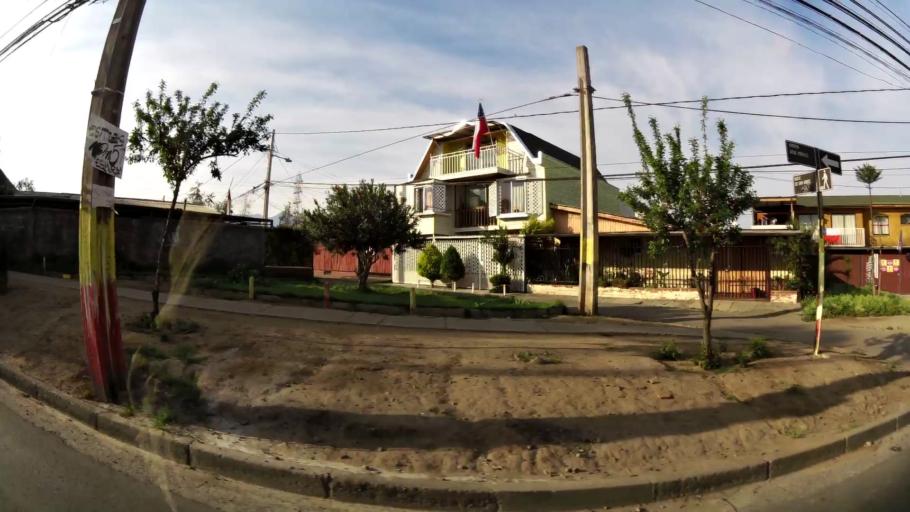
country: CL
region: Santiago Metropolitan
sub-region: Provincia de Cordillera
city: Puente Alto
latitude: -33.5590
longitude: -70.5553
